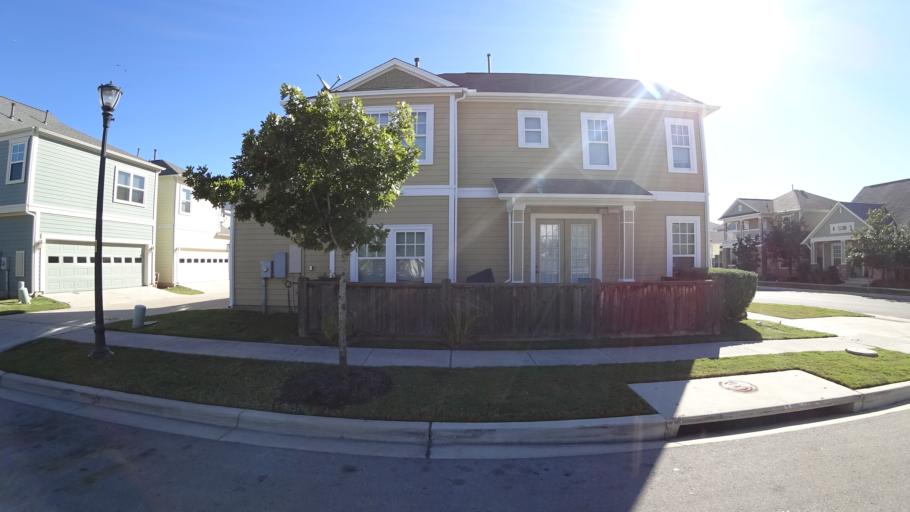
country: US
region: Texas
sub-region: Travis County
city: Austin
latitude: 30.2975
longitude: -97.7020
